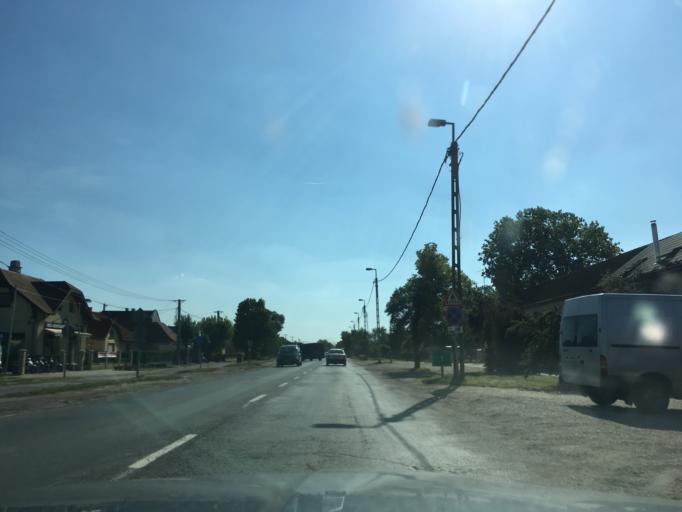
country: HU
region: Hajdu-Bihar
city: Debrecen
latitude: 47.5473
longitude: 21.6543
